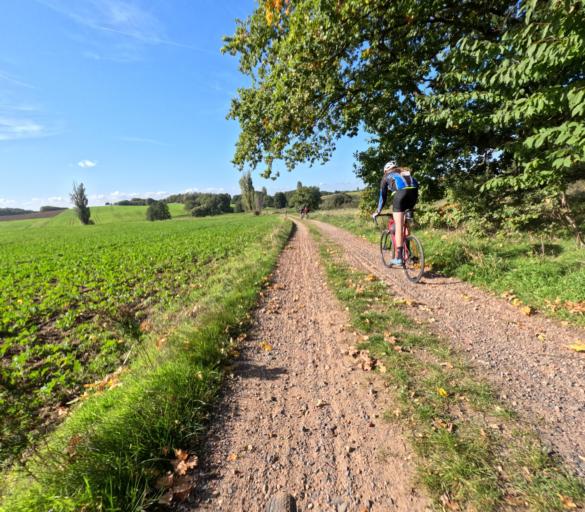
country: DE
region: Saxony
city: Radeburg
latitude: 51.1677
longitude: 13.7426
